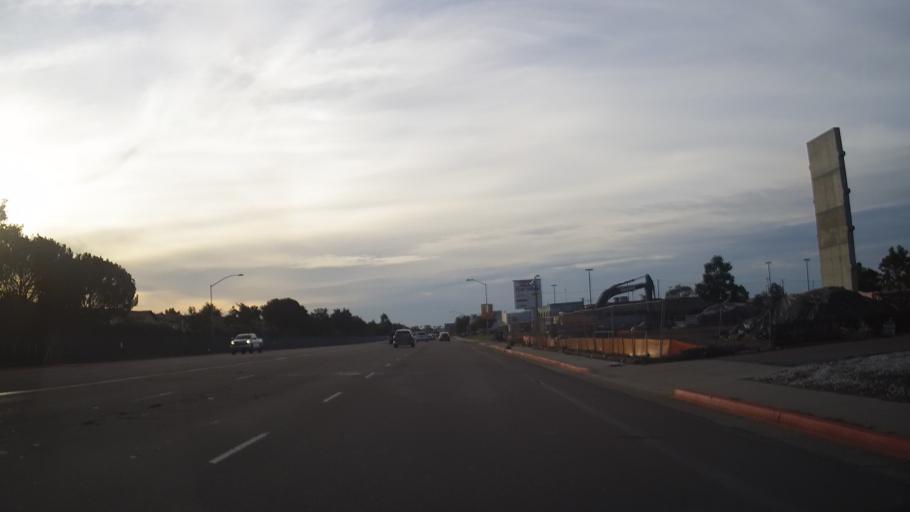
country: US
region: California
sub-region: San Diego County
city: Poway
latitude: 32.8939
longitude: -117.1258
